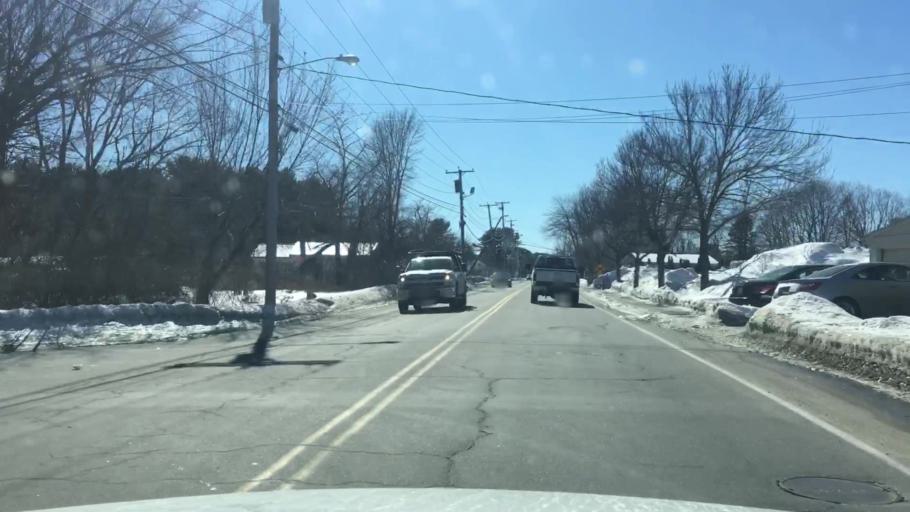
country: US
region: Maine
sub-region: Sagadahoc County
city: Topsham
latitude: 43.9118
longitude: -69.9879
